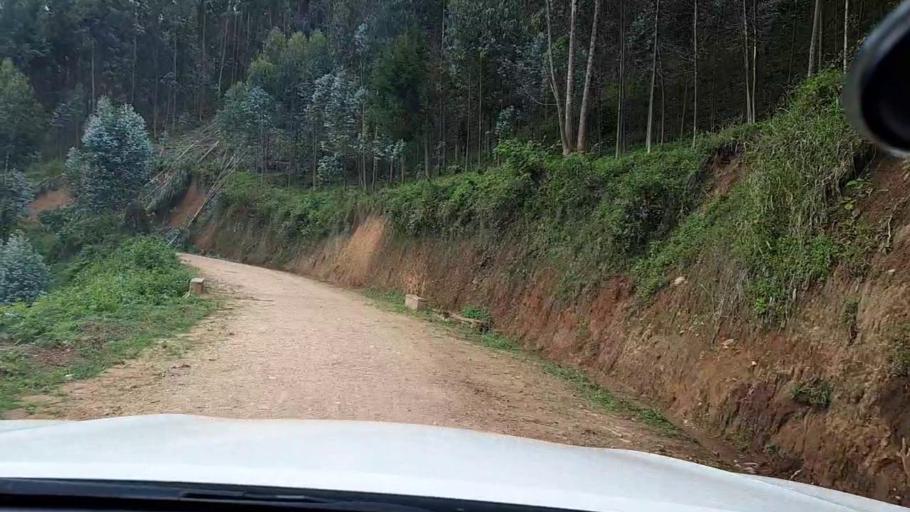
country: RW
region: Western Province
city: Kibuye
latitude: -2.2815
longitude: 29.3024
